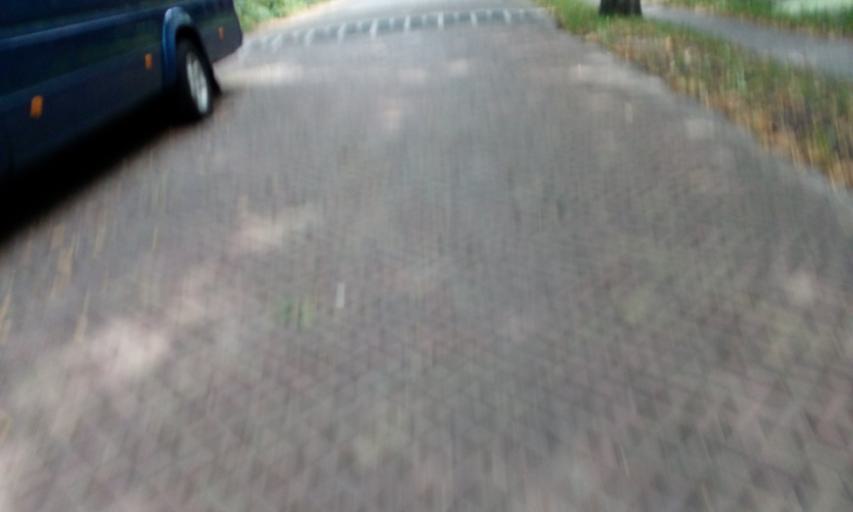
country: NL
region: South Holland
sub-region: Gemeente Rijswijk
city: Rijswijk
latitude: 52.0475
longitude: 4.3190
